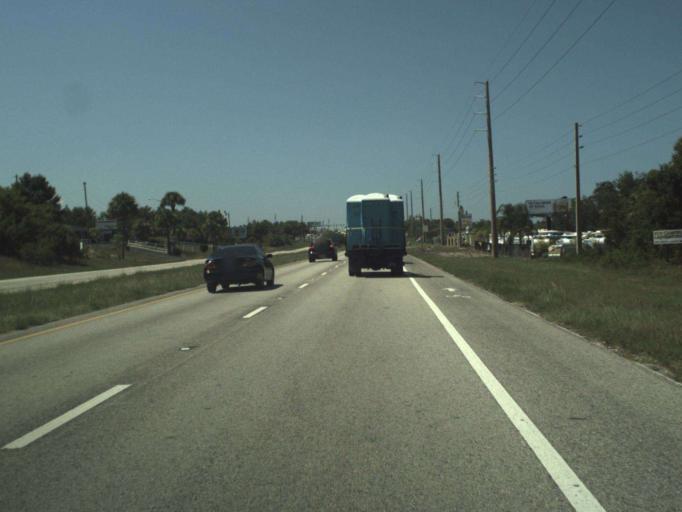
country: US
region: Florida
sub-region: Saint Lucie County
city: Fort Pierce North
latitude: 27.4941
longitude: -80.3439
